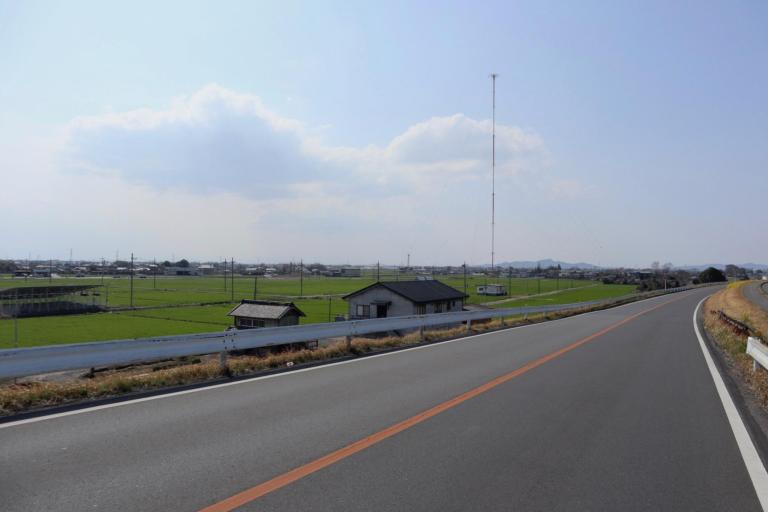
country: JP
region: Tochigi
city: Ashikaga
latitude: 36.3016
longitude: 139.4960
